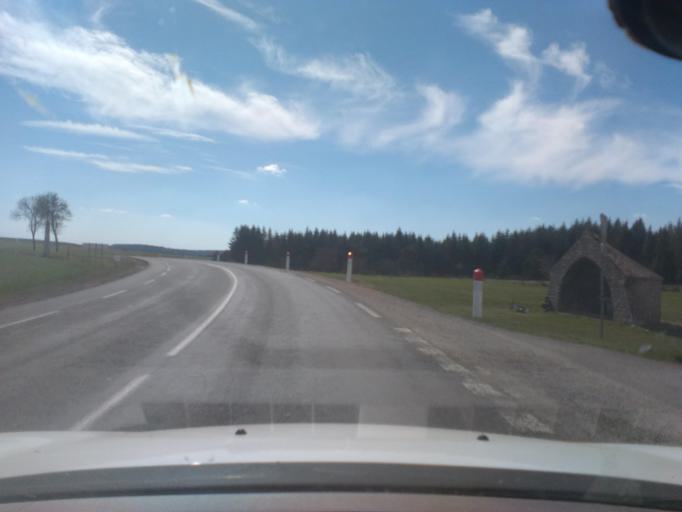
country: FR
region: Languedoc-Roussillon
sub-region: Departement de la Lozere
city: Mende
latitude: 44.5882
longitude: 3.6595
